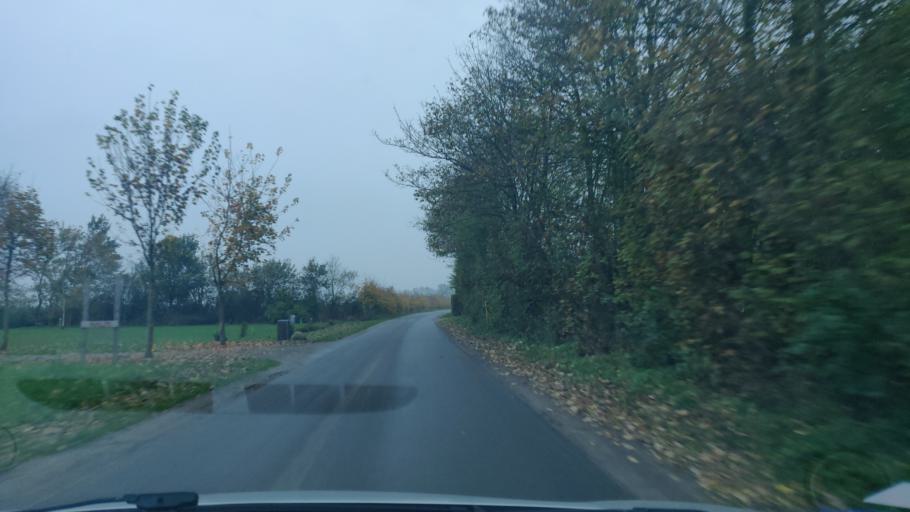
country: DK
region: South Denmark
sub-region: Kolding Kommune
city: Kolding
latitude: 55.5763
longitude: 9.4671
